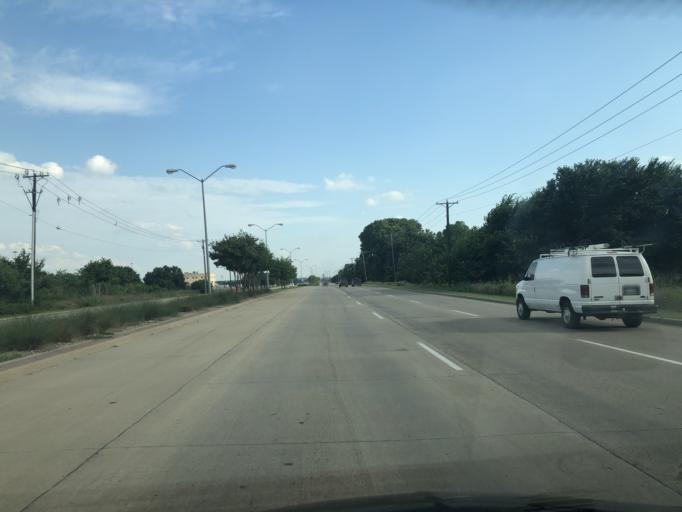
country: US
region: Texas
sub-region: Dallas County
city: Grand Prairie
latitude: 32.7850
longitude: -96.9948
